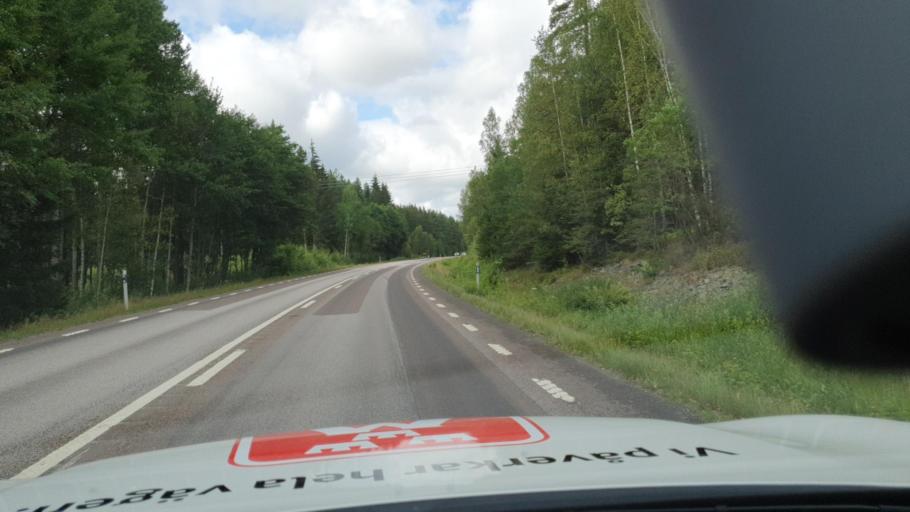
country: SE
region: Vaestra Goetaland
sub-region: Amals Kommun
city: Amal
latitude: 59.0603
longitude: 12.6536
